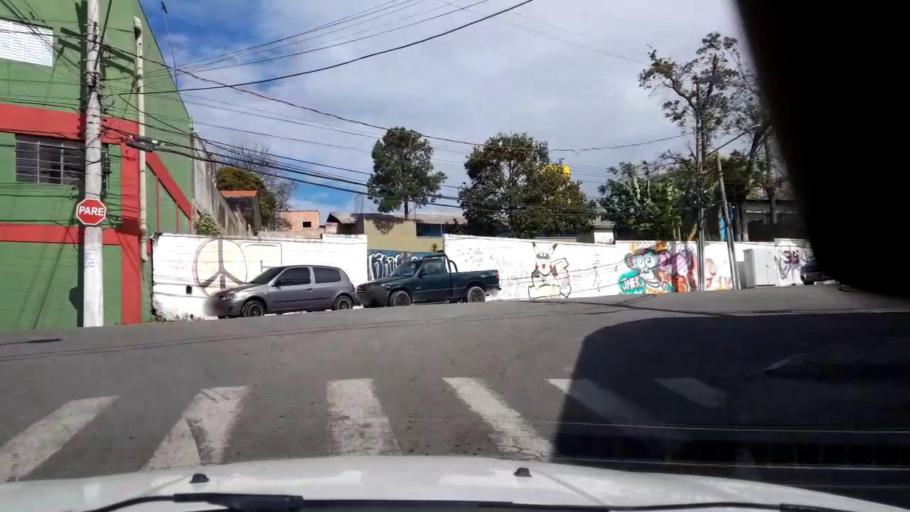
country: BR
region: Sao Paulo
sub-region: Ferraz De Vasconcelos
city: Ferraz de Vasconcelos
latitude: -23.5318
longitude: -46.3922
